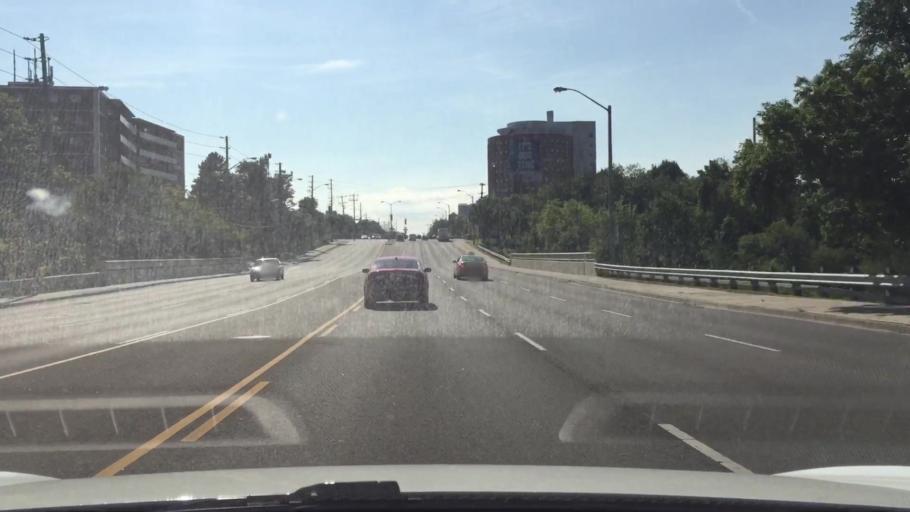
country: CA
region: Ontario
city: Scarborough
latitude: 43.7566
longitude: -79.2424
